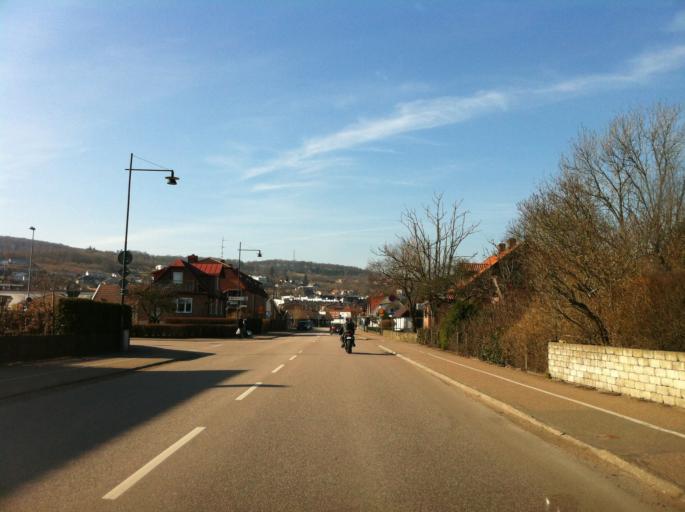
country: SE
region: Skane
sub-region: Bastads Kommun
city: Bastad
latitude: 56.4270
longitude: 12.8517
